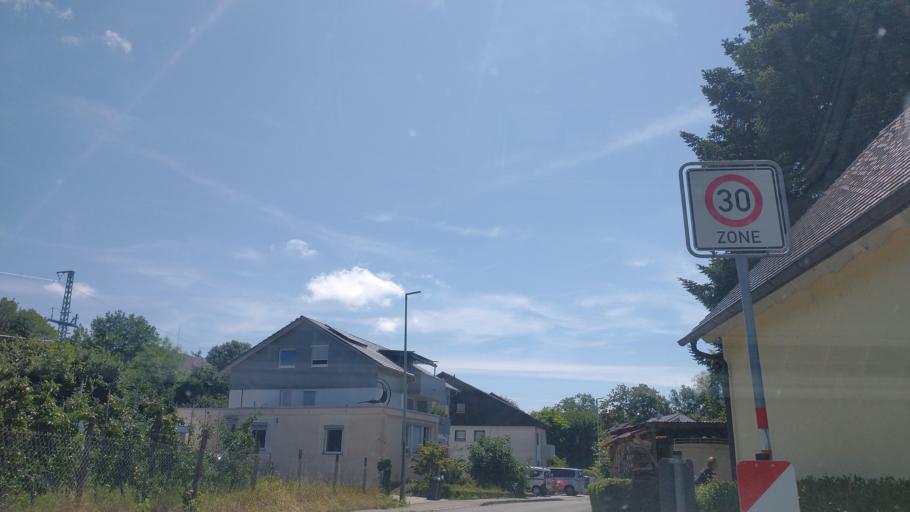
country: DE
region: Baden-Wuerttemberg
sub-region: Tuebingen Region
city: Kressbronn am Bodensee
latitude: 47.5946
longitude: 9.5975
